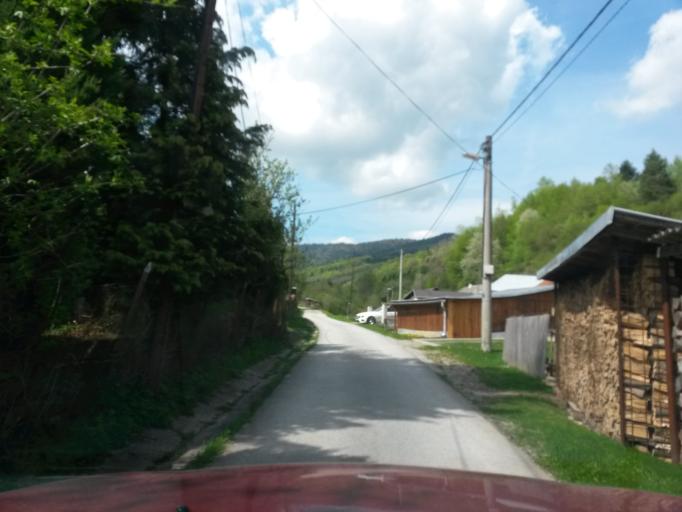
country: SK
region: Kosicky
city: Krompachy
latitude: 48.8122
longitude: 20.8071
